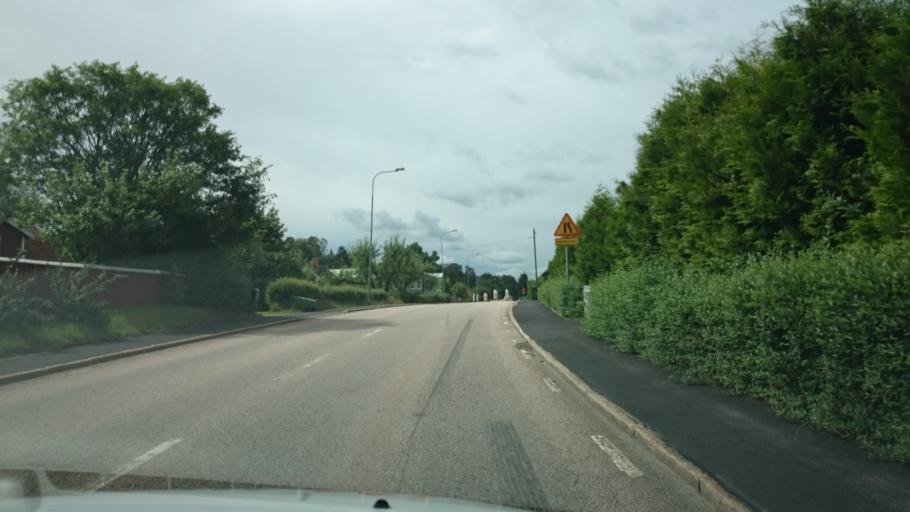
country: SE
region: Halland
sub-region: Hylte Kommun
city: Hyltebruk
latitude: 56.9952
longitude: 13.2343
